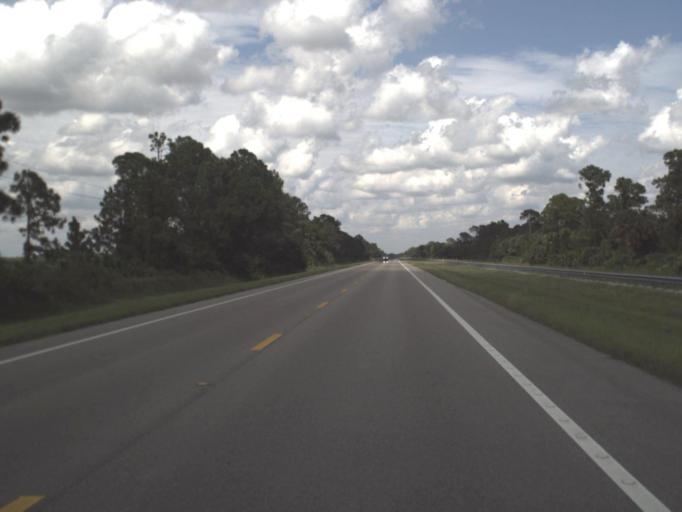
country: US
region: Florida
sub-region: Collier County
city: Immokalee
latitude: 26.3300
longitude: -81.3432
